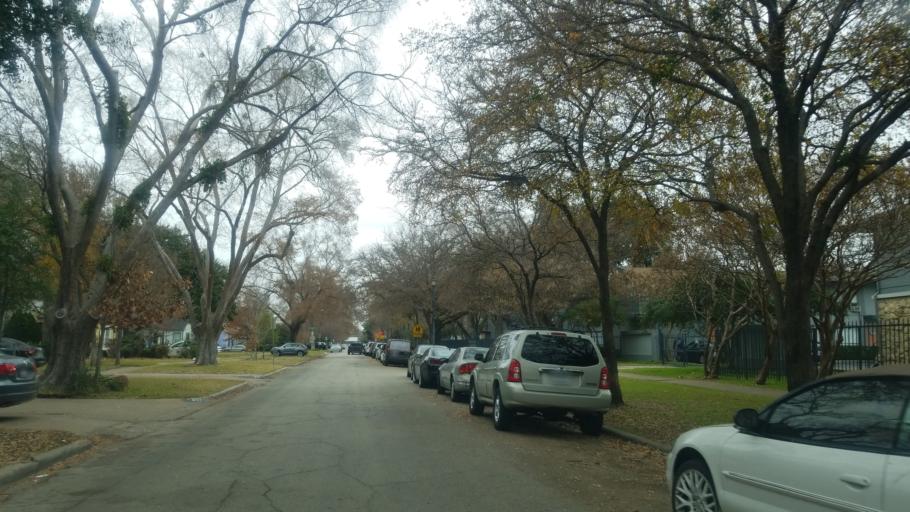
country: US
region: Texas
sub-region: Dallas County
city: Highland Park
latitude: 32.8245
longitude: -96.8281
